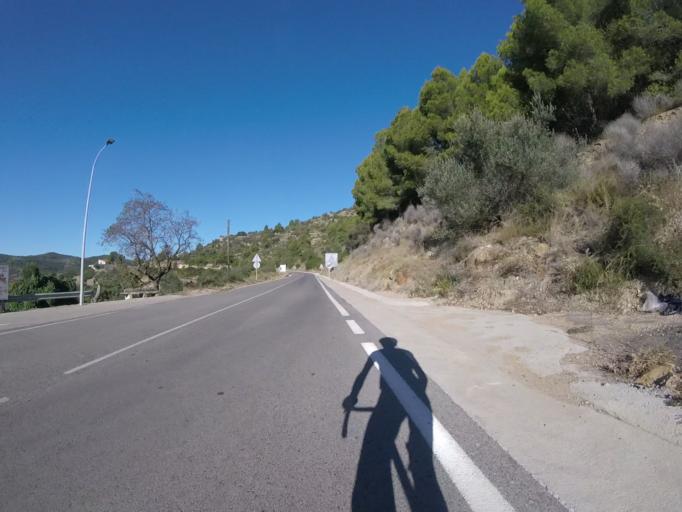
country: ES
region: Valencia
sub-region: Provincia de Castello
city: Cervera del Maestre
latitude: 40.4568
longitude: 0.2730
